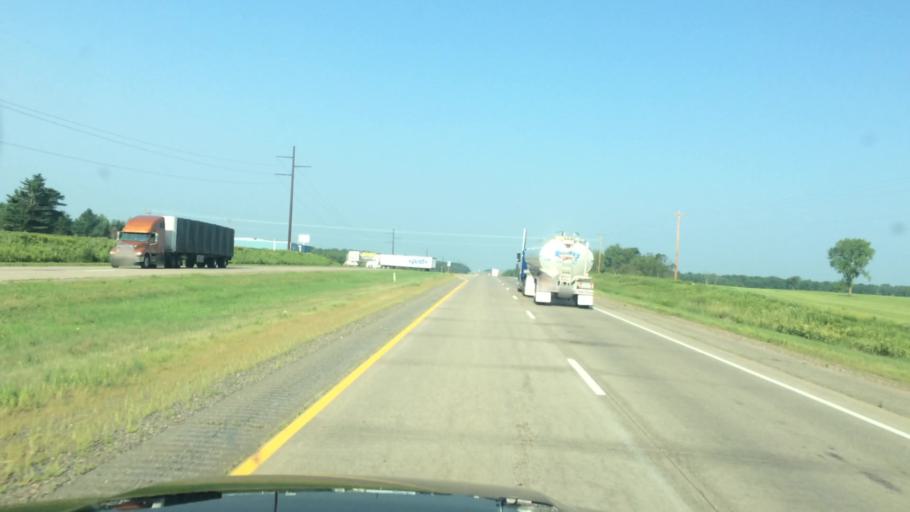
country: US
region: Wisconsin
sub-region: Marathon County
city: Edgar
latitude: 44.9444
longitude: -90.0014
